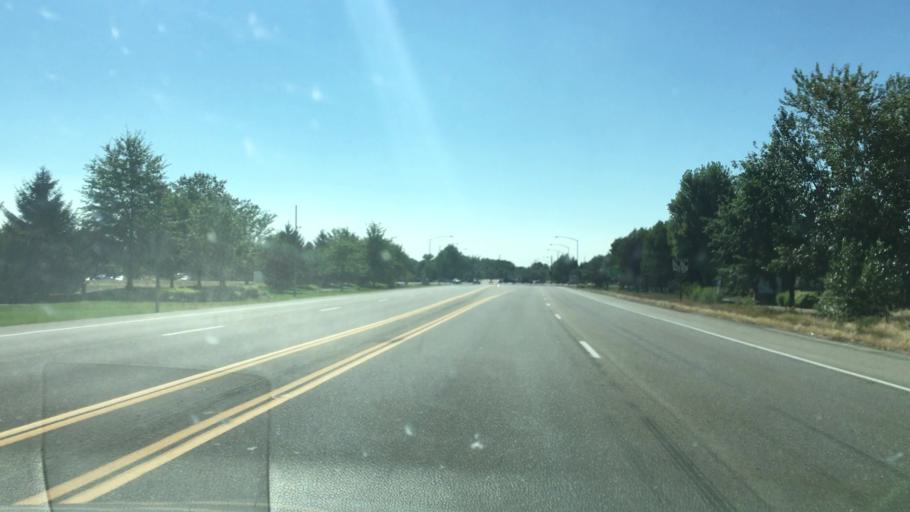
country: US
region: Idaho
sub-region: Ada County
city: Eagle
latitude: 43.6905
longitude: -116.3498
